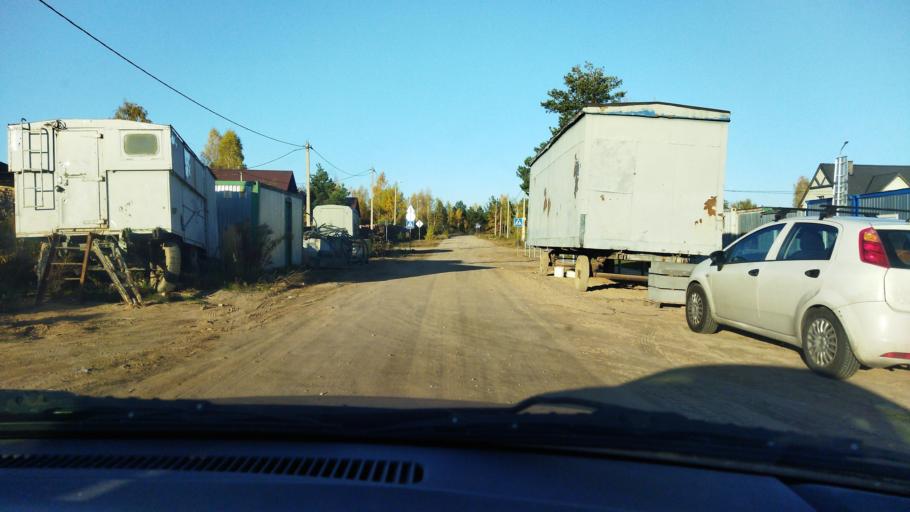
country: BY
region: Minsk
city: Kalodzishchy
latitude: 53.9129
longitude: 27.7708
